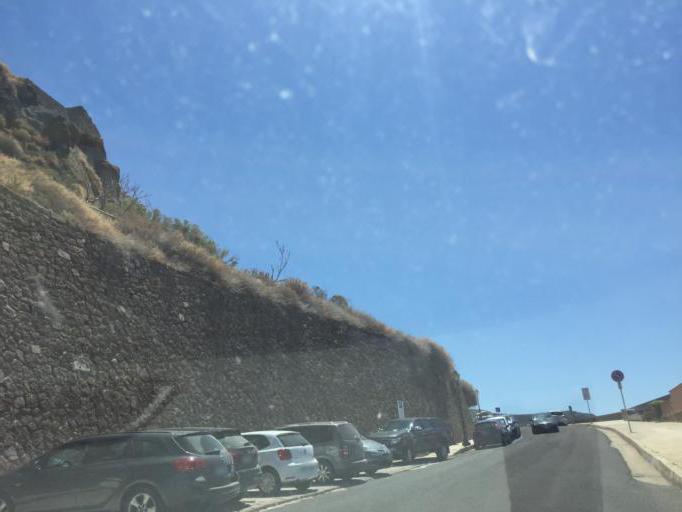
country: IT
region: Sardinia
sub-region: Provincia di Sassari
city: Castelsardo
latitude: 40.9159
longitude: 8.7112
